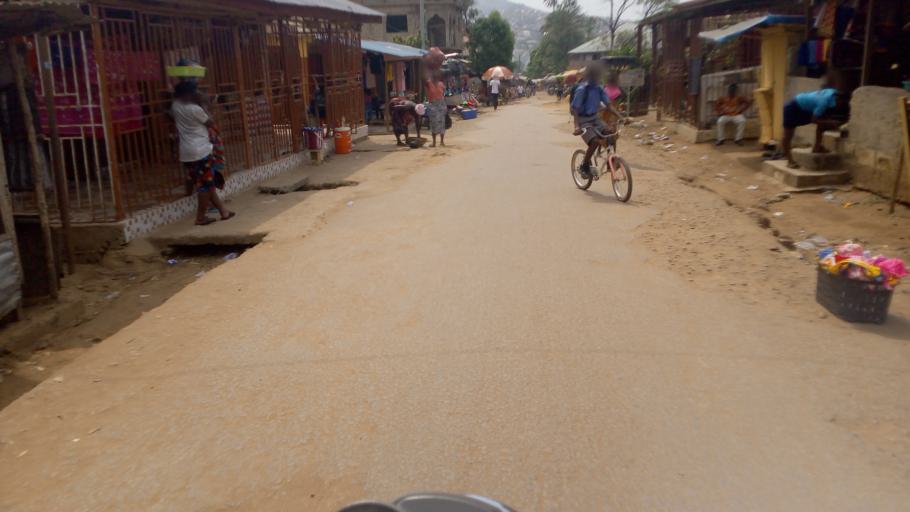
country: SL
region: Western Area
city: Waterloo
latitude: 8.3245
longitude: -13.0657
